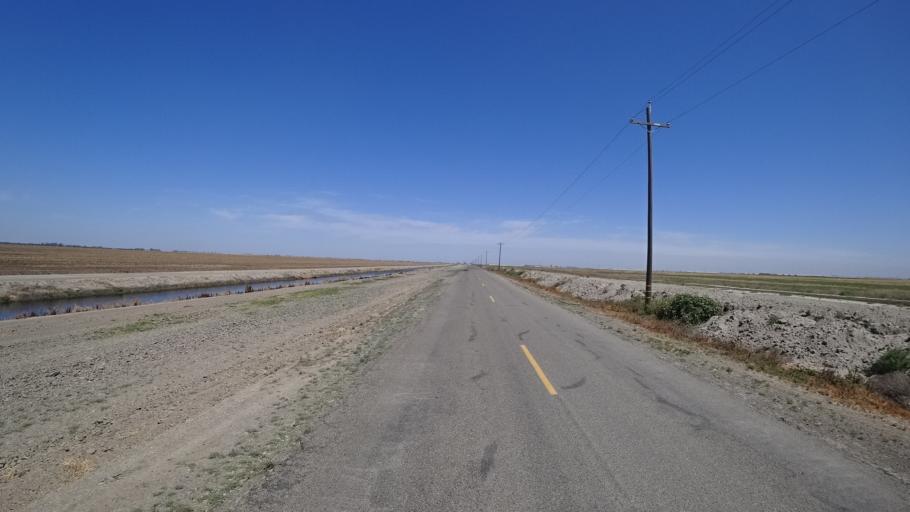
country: US
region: California
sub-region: Kings County
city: Stratford
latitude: 36.1618
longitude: -119.7174
